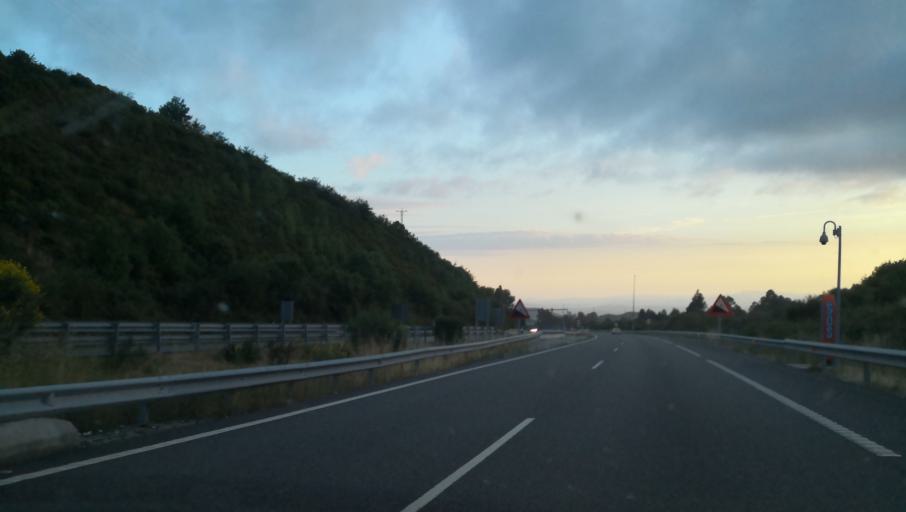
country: ES
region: Galicia
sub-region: Provincia de Pontevedra
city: Covelo
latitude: 42.1737
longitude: -8.3696
